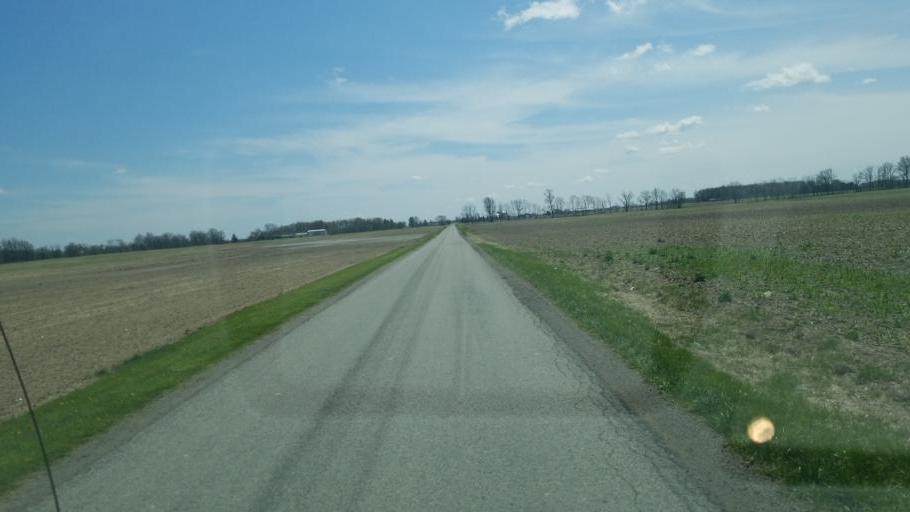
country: US
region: Ohio
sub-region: Union County
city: Richwood
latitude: 40.4616
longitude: -83.2504
